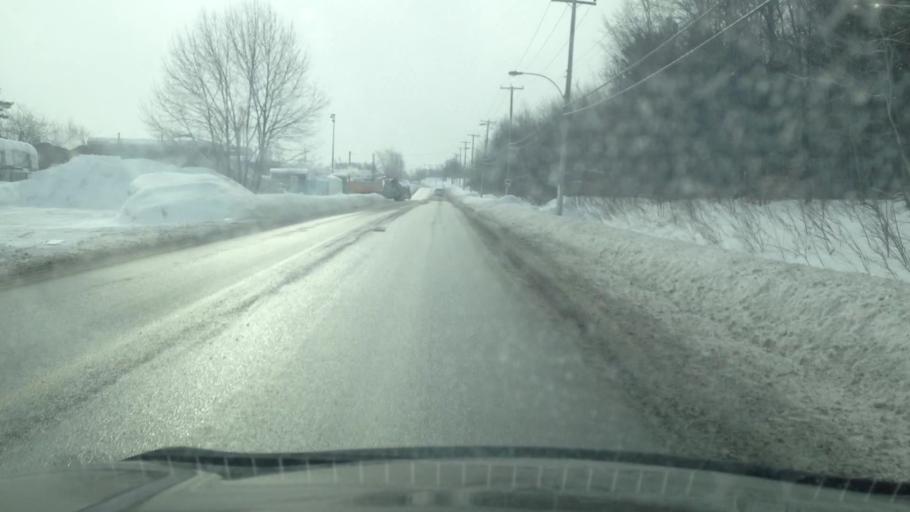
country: CA
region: Quebec
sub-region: Laurentides
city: Saint-Jerome
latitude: 45.7912
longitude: -74.0285
